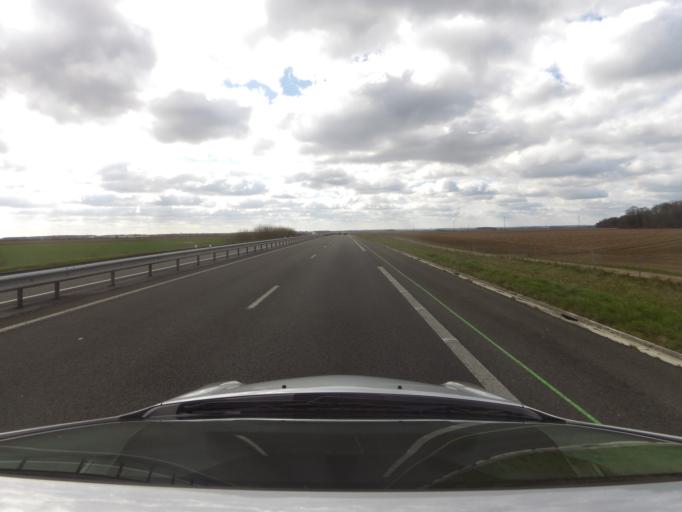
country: FR
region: Picardie
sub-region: Departement de la Somme
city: Nouvion
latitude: 50.2260
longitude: 1.7521
